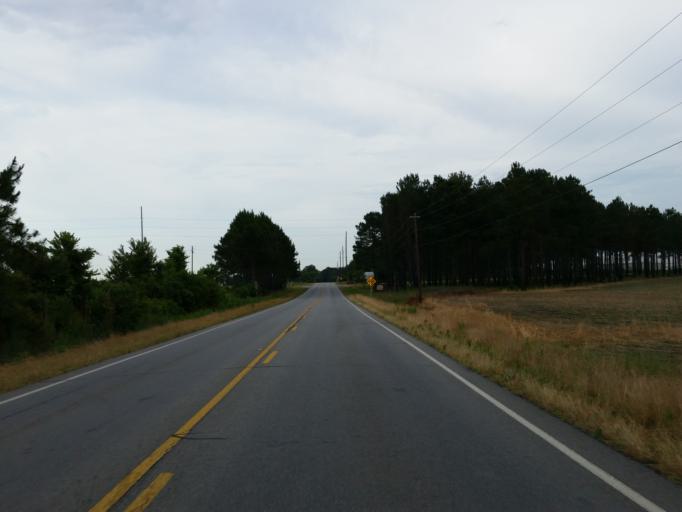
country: US
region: Georgia
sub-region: Dooly County
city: Vienna
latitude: 32.0731
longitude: -83.7966
